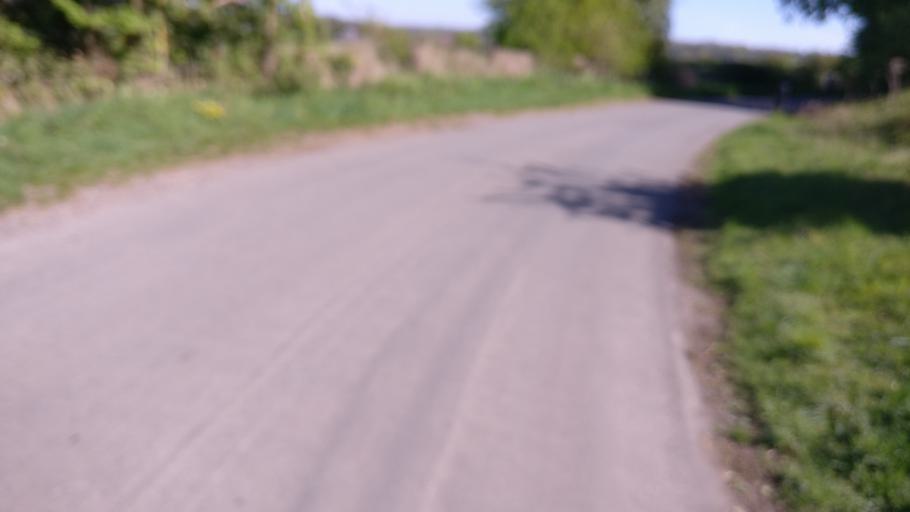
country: GB
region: England
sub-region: Hampshire
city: Basingstoke
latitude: 51.2375
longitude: -1.0871
